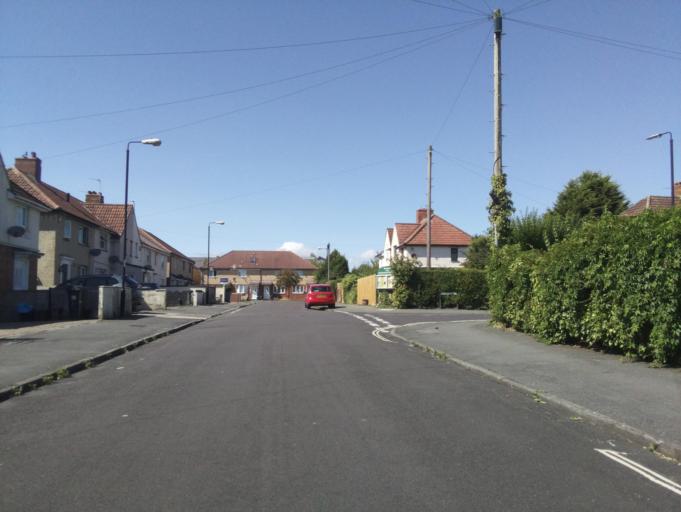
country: GB
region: England
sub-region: Bristol
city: Bristol
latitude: 51.5052
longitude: -2.5931
